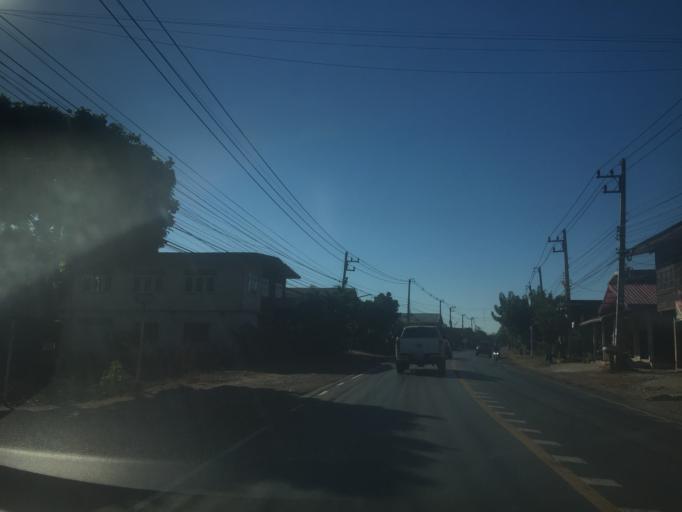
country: TH
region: Changwat Udon Thani
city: Si That
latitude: 16.9752
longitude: 103.2027
